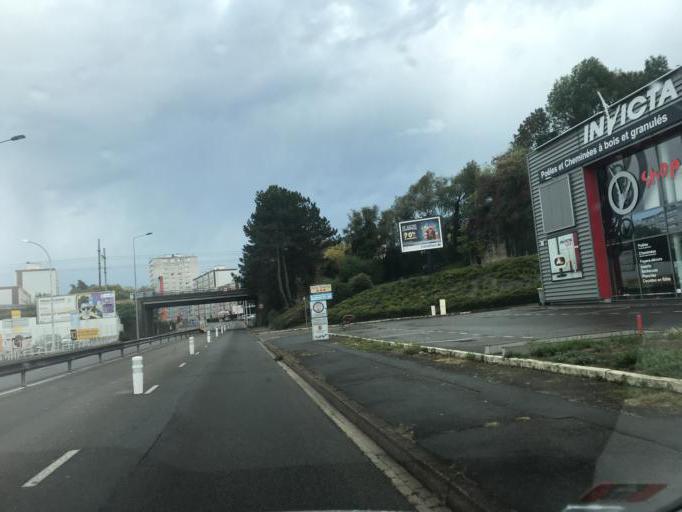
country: FR
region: Rhone-Alpes
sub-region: Departement de l'Ain
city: Bourg-en-Bresse
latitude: 46.2127
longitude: 5.2183
